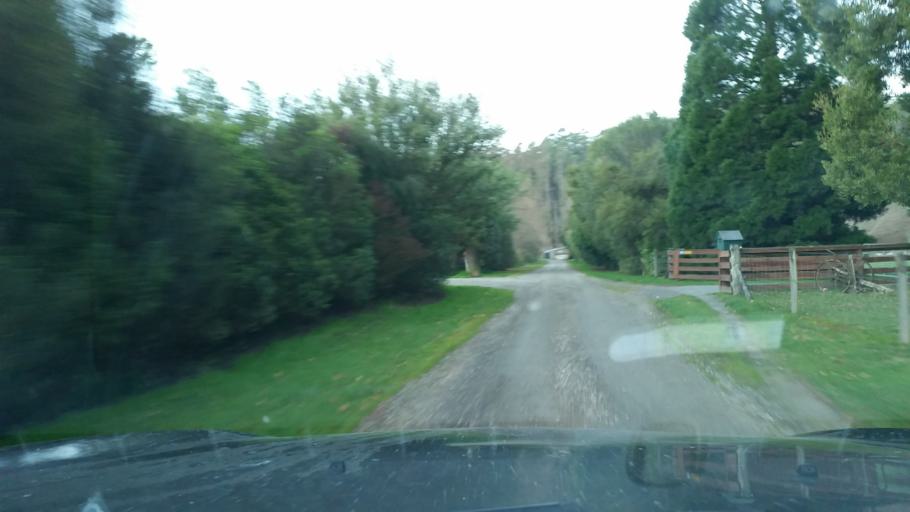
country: NZ
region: Marlborough
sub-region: Marlborough District
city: Blenheim
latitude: -41.4736
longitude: 173.7416
